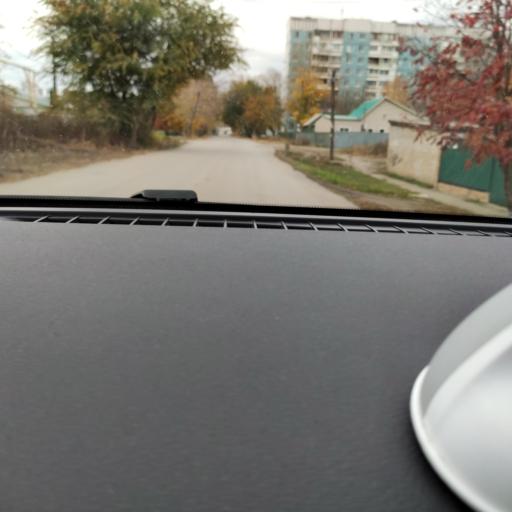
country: RU
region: Samara
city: Petra-Dubrava
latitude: 53.2430
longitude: 50.3143
